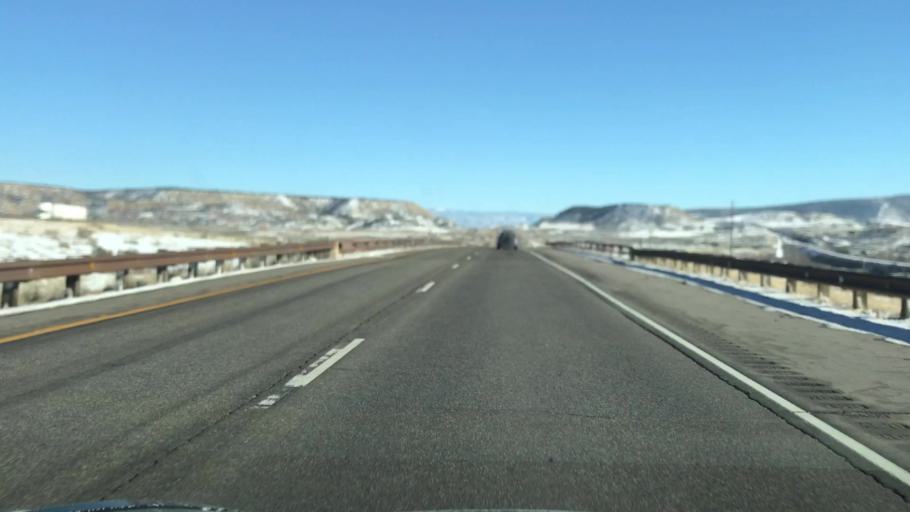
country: US
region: Colorado
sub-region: Garfield County
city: Rifle
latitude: 39.5008
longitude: -107.9082
